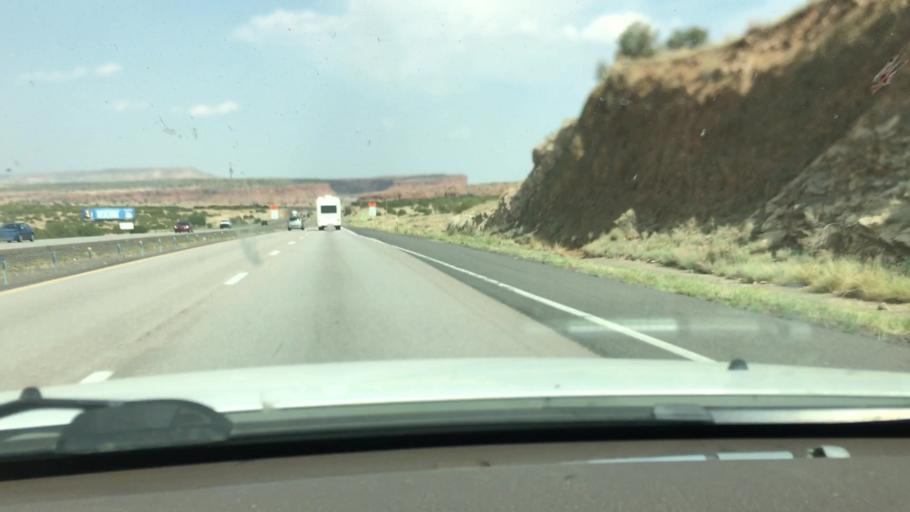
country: US
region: New Mexico
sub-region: Cibola County
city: Laguna
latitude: 35.0378
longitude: -107.3592
